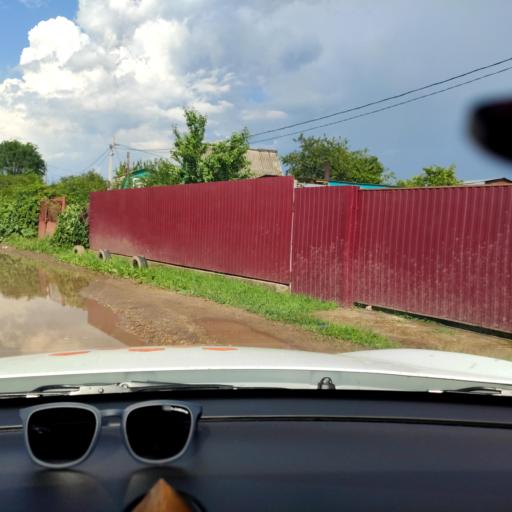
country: RU
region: Tatarstan
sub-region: Zelenodol'skiy Rayon
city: Vasil'yevo
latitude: 55.8238
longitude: 48.7240
